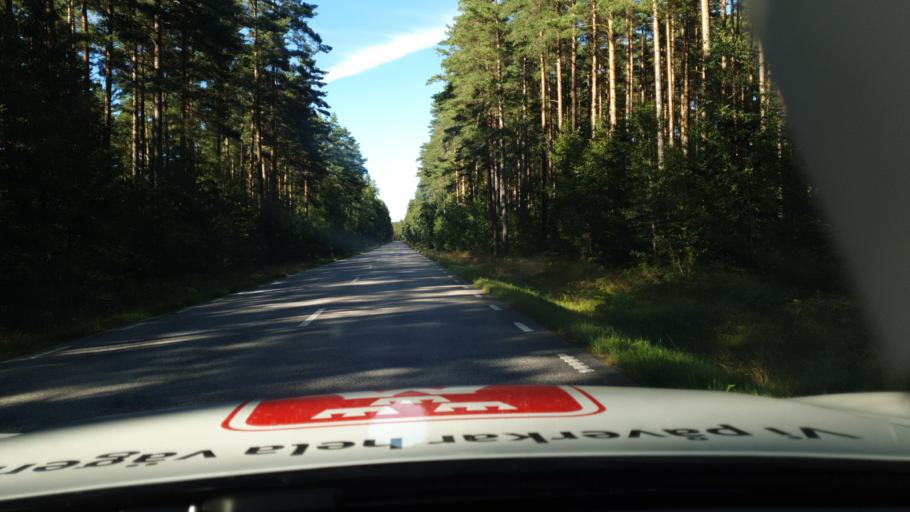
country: SE
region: Vaestra Goetaland
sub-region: Skovde Kommun
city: Stopen
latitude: 58.4577
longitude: 13.9562
